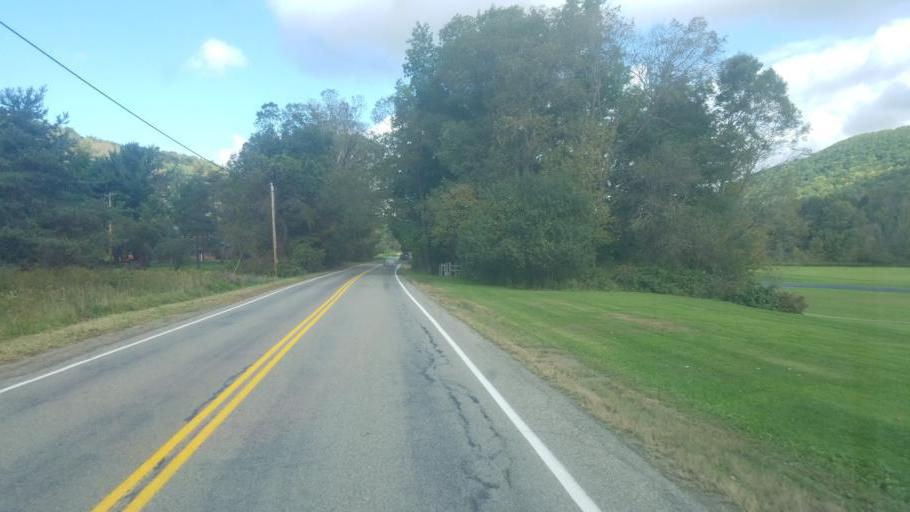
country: US
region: New York
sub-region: Allegany County
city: Cuba
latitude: 42.2202
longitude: -78.3113
